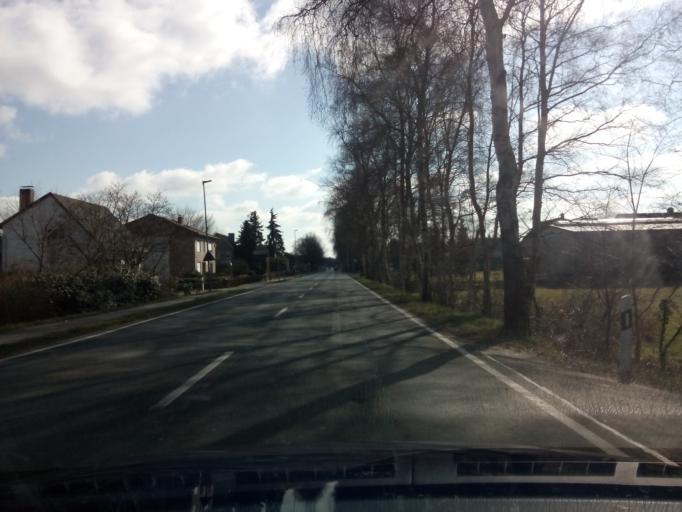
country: DE
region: Lower Saxony
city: Grasberg
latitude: 53.1883
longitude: 8.9805
